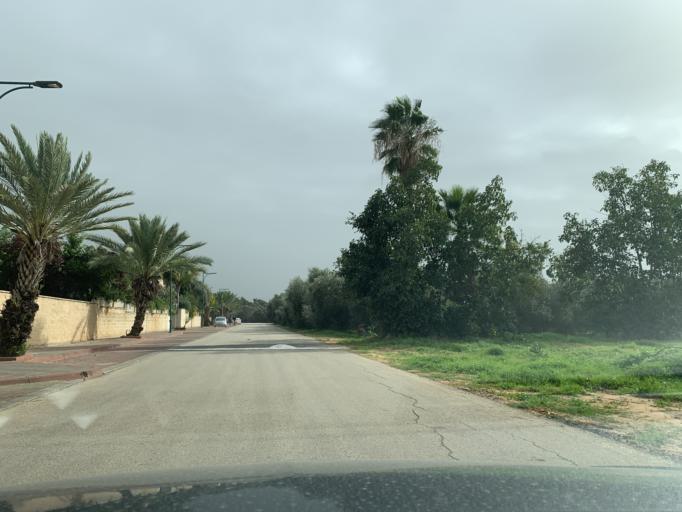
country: IL
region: Central District
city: Jaljulya
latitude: 32.1566
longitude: 34.9414
